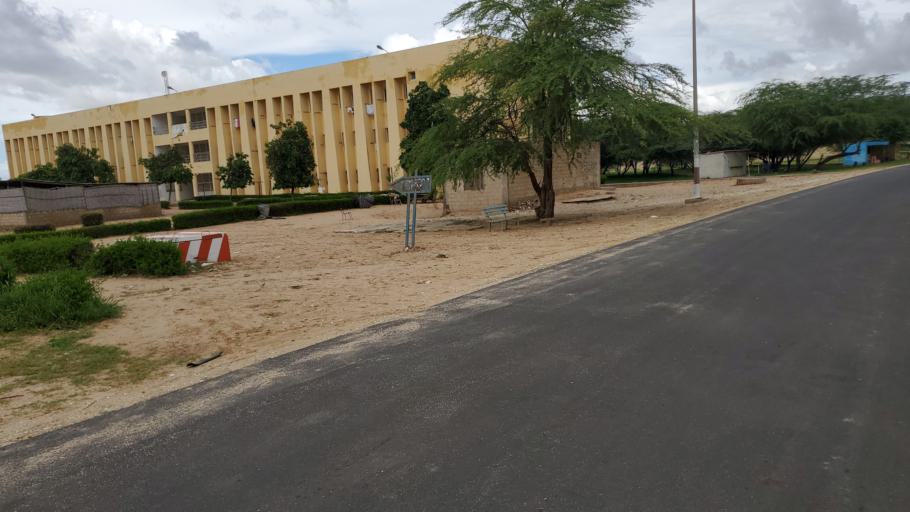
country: SN
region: Saint-Louis
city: Saint-Louis
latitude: 16.0673
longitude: -16.4237
